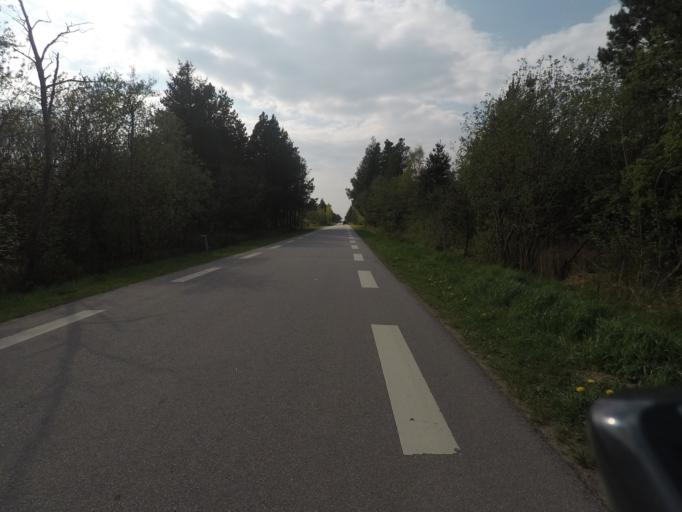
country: DE
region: Schleswig-Holstein
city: List
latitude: 55.1295
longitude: 8.5315
